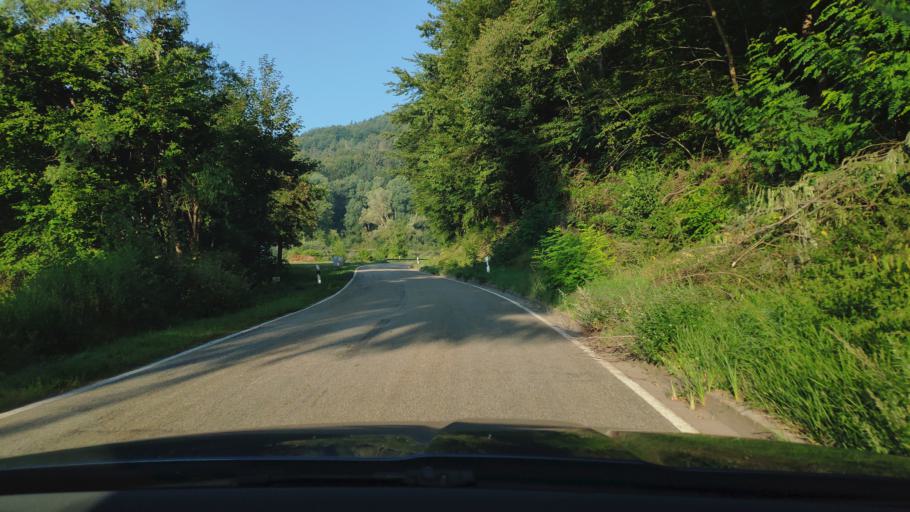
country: DE
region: Rheinland-Pfalz
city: Hirschthal
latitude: 49.0610
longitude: 7.7390
